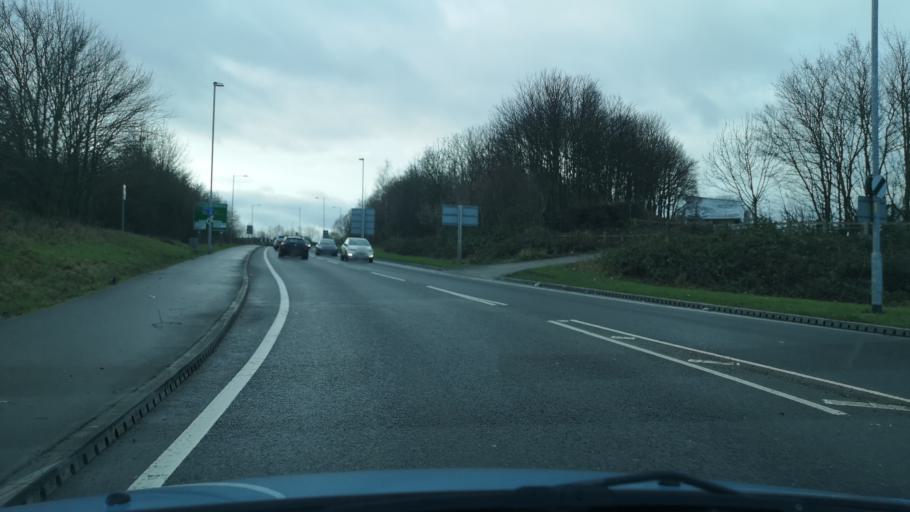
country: GB
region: England
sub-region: City and Borough of Wakefield
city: Hemsworth
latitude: 53.6050
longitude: -1.3399
